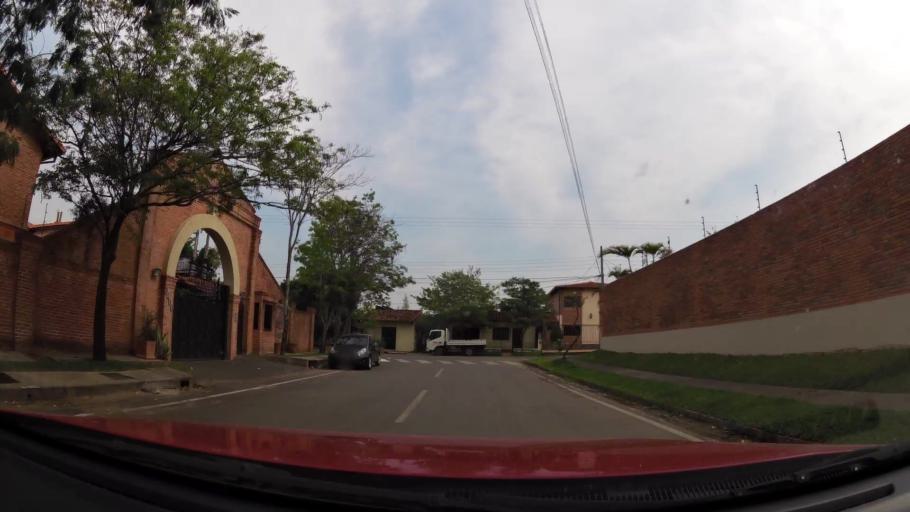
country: PY
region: Central
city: Fernando de la Mora
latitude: -25.2811
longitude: -57.5499
